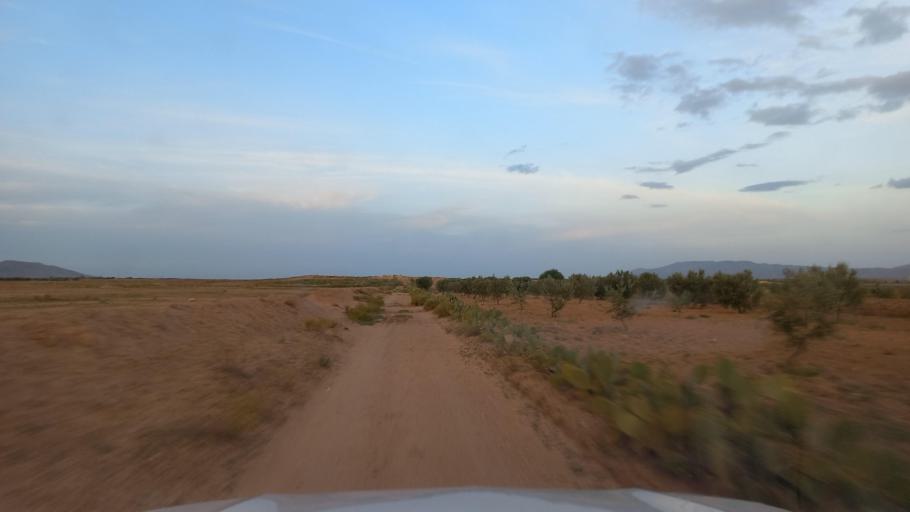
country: TN
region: Al Qasrayn
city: Sbiba
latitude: 35.3510
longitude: 9.0253
